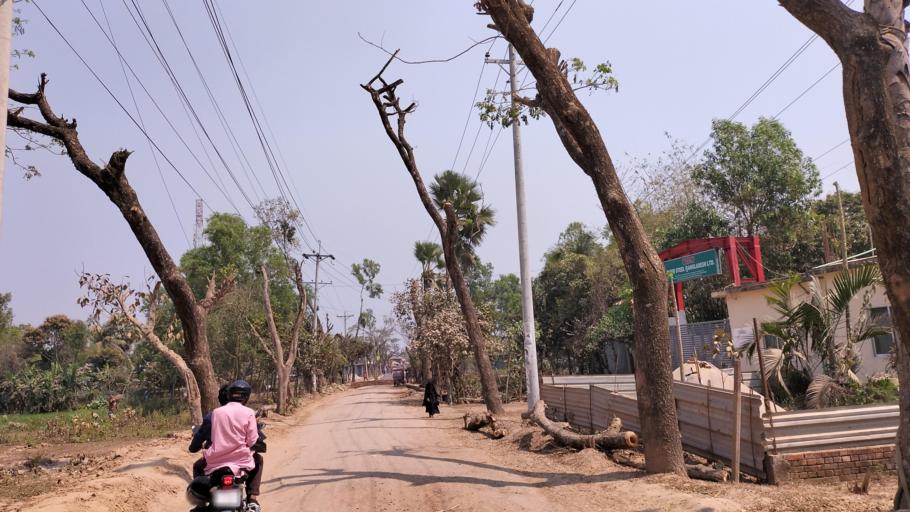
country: BD
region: Dhaka
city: Sakhipur
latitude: 24.3071
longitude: 90.3124
